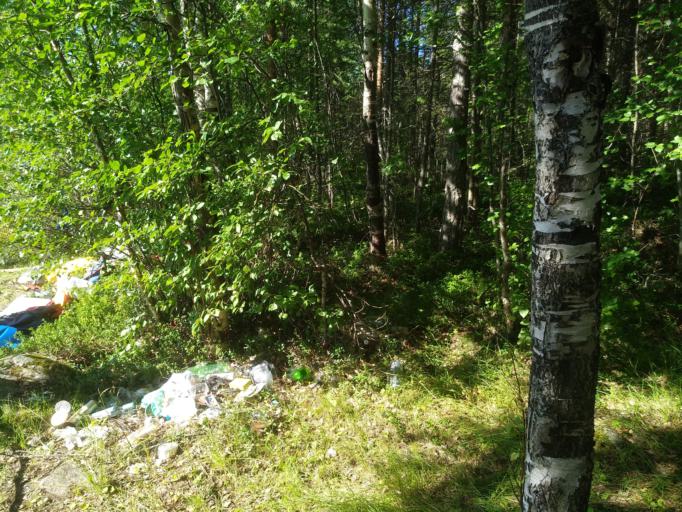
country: RU
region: Republic of Karelia
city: Kalevala
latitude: 65.0851
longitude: 31.1026
